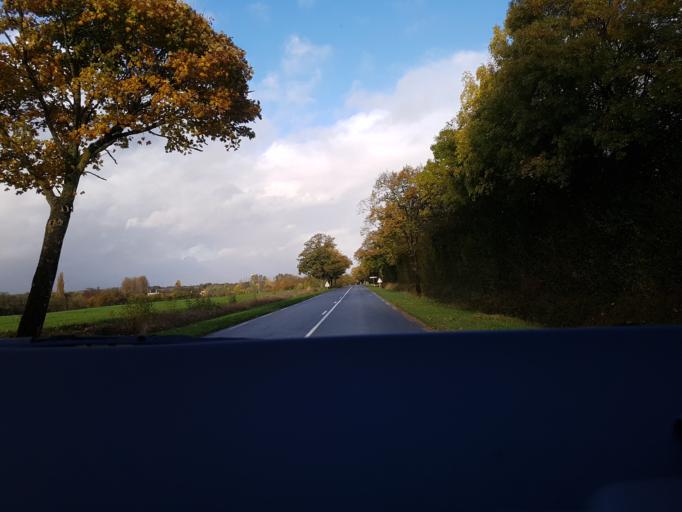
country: FR
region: Poitou-Charentes
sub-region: Departement des Deux-Sevres
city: Brioux-sur-Boutonne
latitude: 46.1183
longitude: -0.2424
